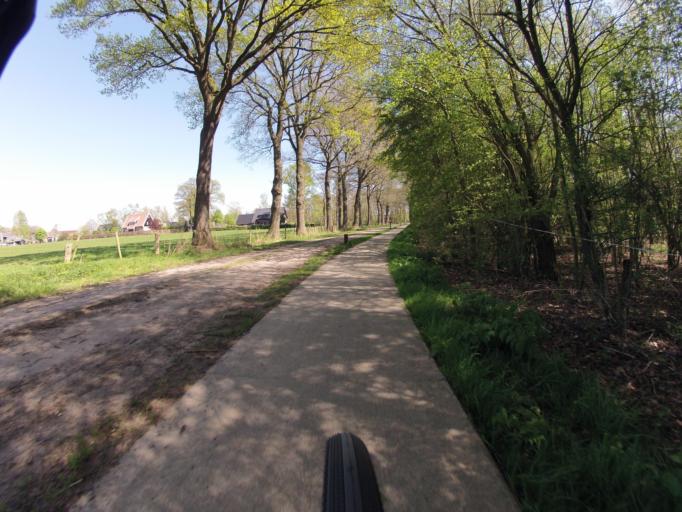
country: NL
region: Overijssel
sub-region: Gemeente Losser
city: Losser
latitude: 52.2670
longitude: 6.9880
